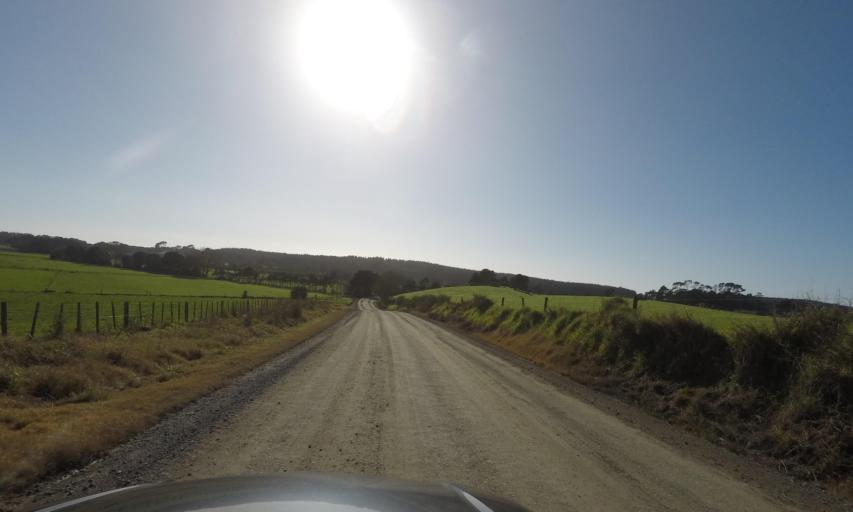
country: NZ
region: Auckland
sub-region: Auckland
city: Wellsford
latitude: -36.1592
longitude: 174.6118
